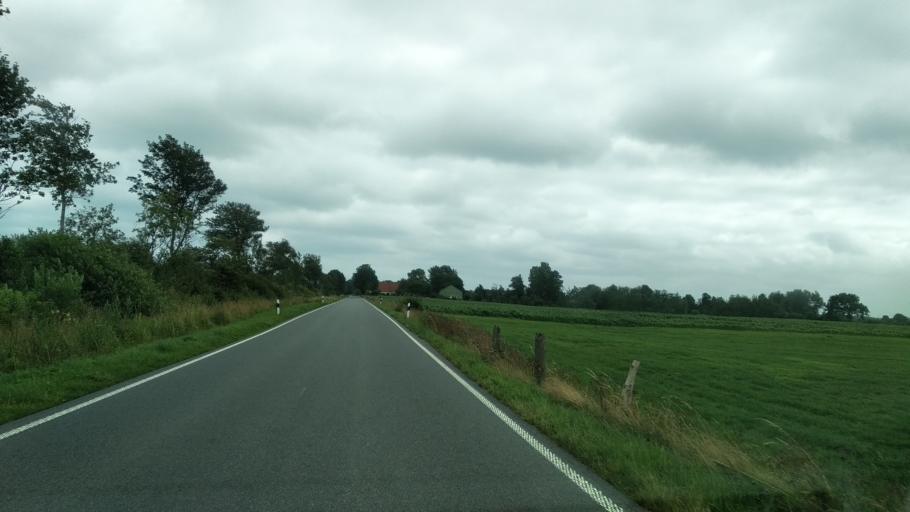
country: DE
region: Schleswig-Holstein
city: Sieverstedt
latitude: 54.6138
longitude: 9.4723
